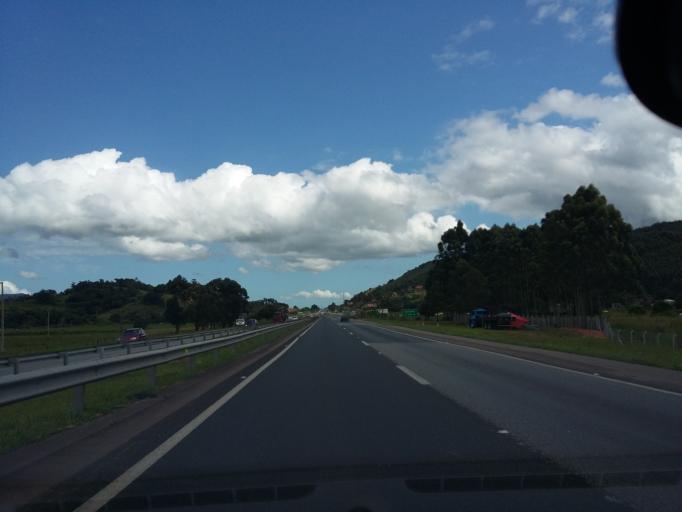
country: BR
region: Santa Catarina
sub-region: Tijucas
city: Tijucas
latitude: -27.2735
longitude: -48.6316
